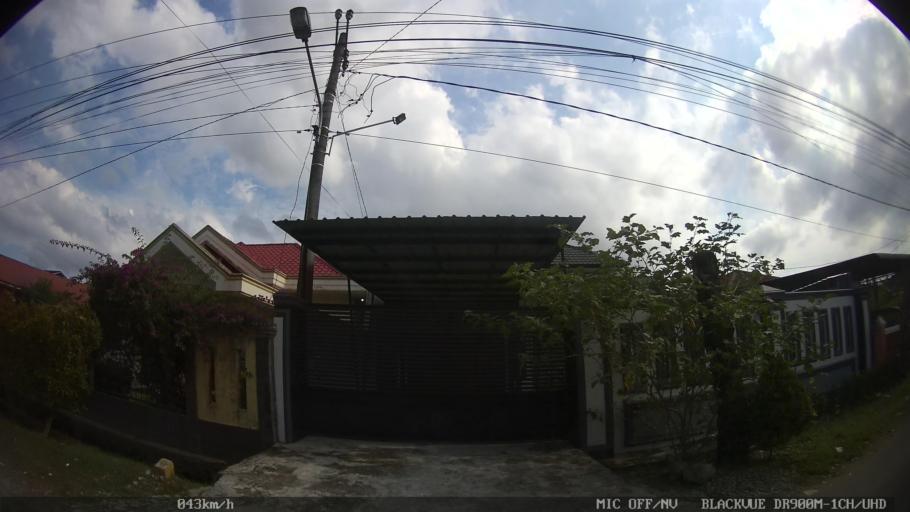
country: ID
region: North Sumatra
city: Medan
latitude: 3.6151
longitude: 98.6559
